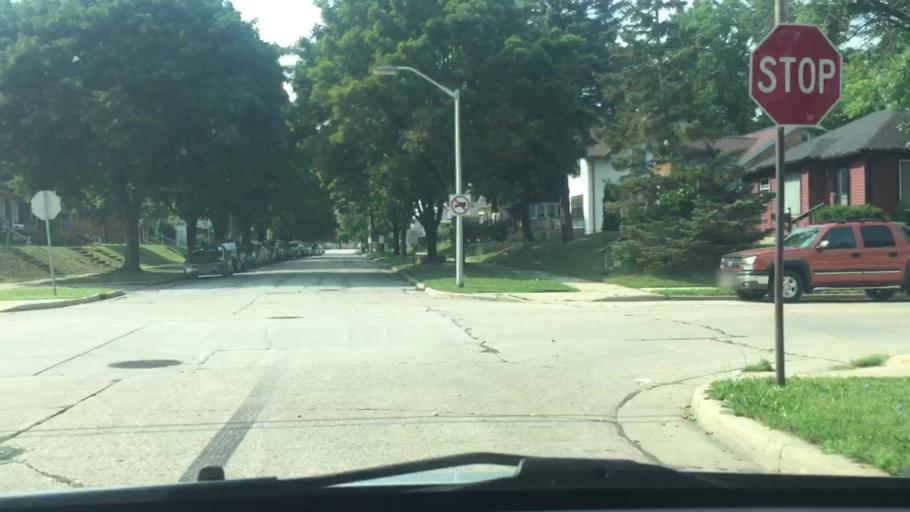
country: US
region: Wisconsin
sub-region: Milwaukee County
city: West Allis
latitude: 43.0131
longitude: -88.0142
